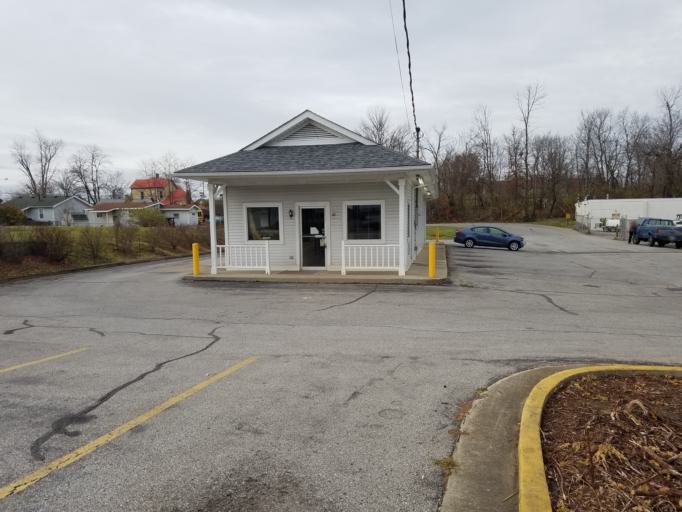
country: US
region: Kentucky
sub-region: Henry County
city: Eminence
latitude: 38.3723
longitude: -85.1792
